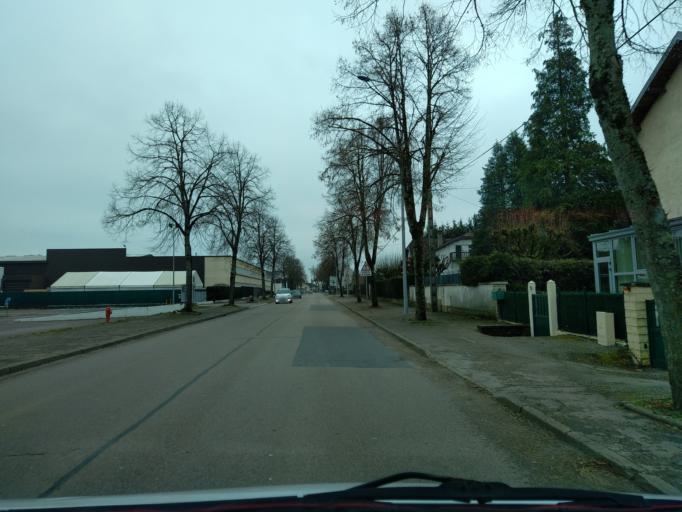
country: FR
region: Franche-Comte
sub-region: Departement de la Haute-Saone
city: Arc-les-Gray
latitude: 47.4586
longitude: 5.5865
